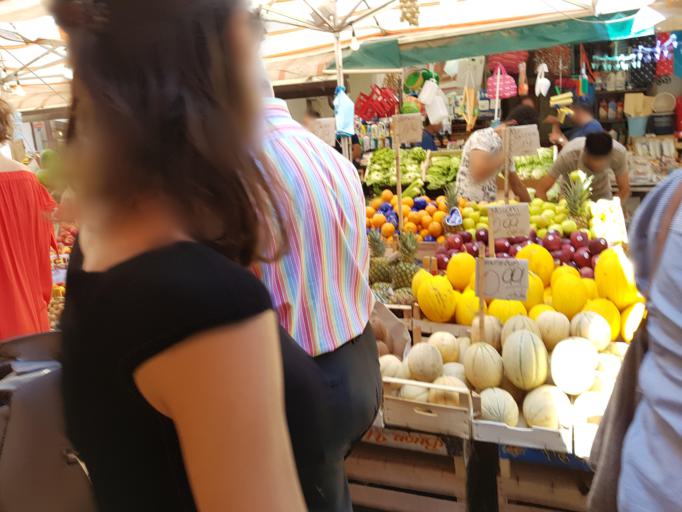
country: IT
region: Sicily
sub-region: Palermo
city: Palermo
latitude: 38.1103
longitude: 13.3636
